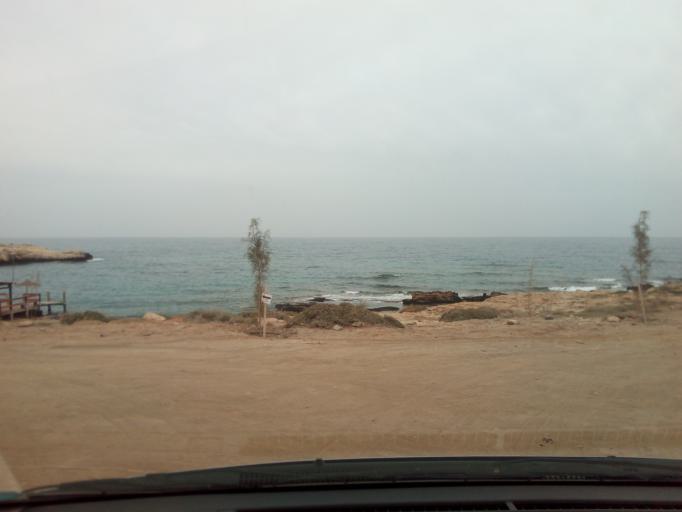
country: CY
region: Ammochostos
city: Paralimni
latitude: 35.0547
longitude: 34.0164
